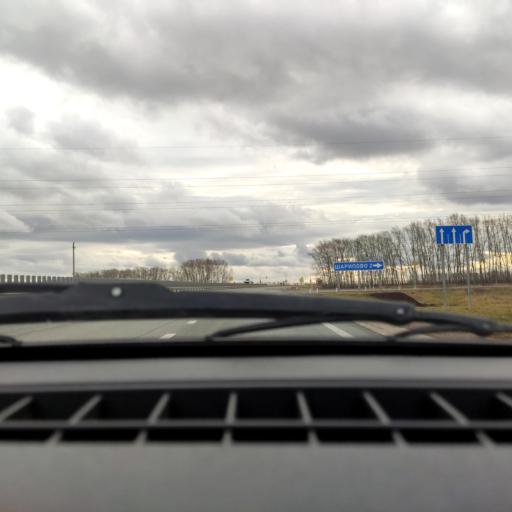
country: RU
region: Bashkortostan
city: Asanovo
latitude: 54.9623
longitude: 55.5848
